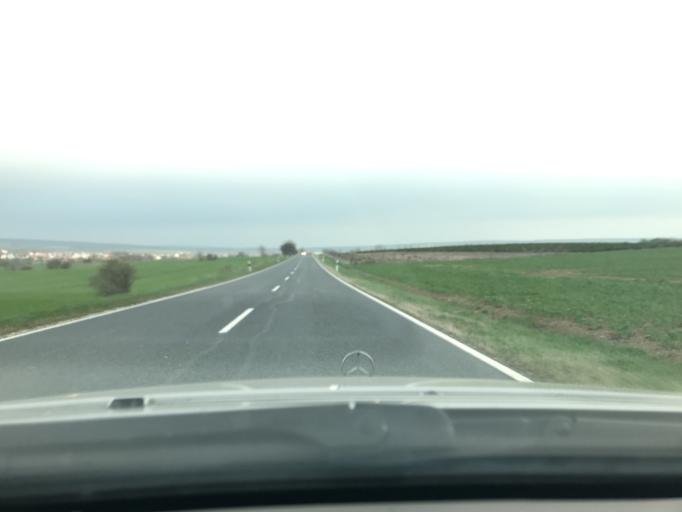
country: DE
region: Thuringia
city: Kefferhausen
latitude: 51.3273
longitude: 10.2951
